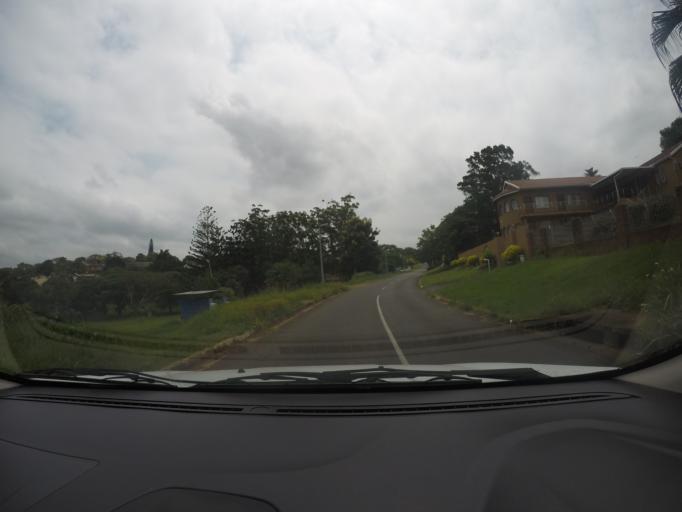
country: ZA
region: KwaZulu-Natal
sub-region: uThungulu District Municipality
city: Empangeni
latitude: -28.7494
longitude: 31.8893
